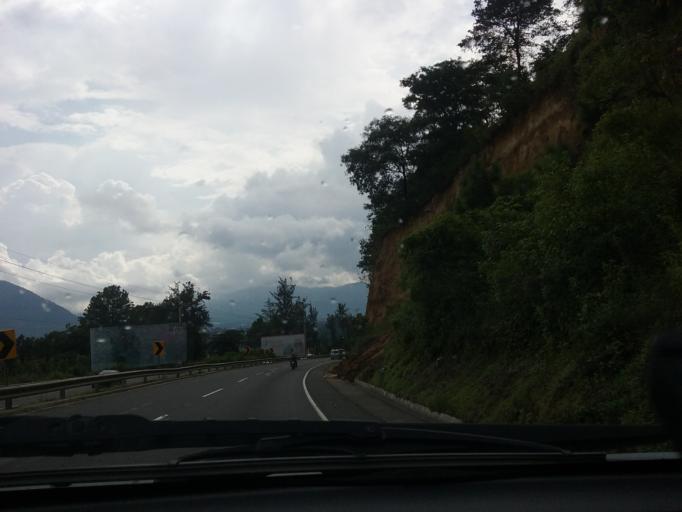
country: GT
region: Sacatepequez
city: Sumpango
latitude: 14.6363
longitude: -90.7447
